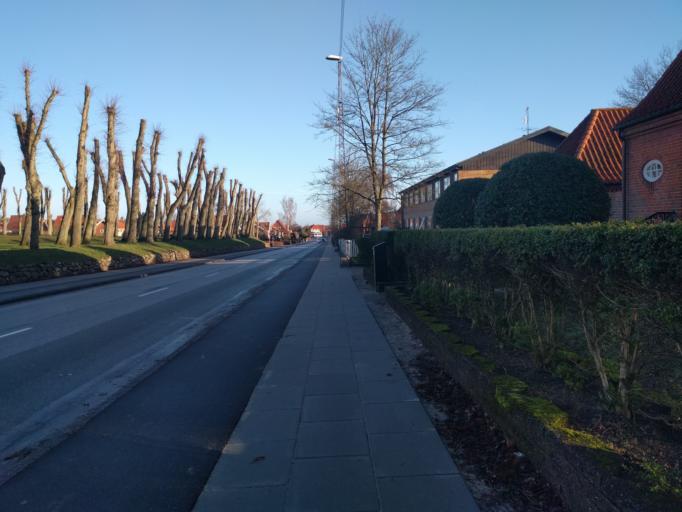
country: DK
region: Central Jutland
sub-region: Viborg Kommune
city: Viborg
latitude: 56.4570
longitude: 9.4139
